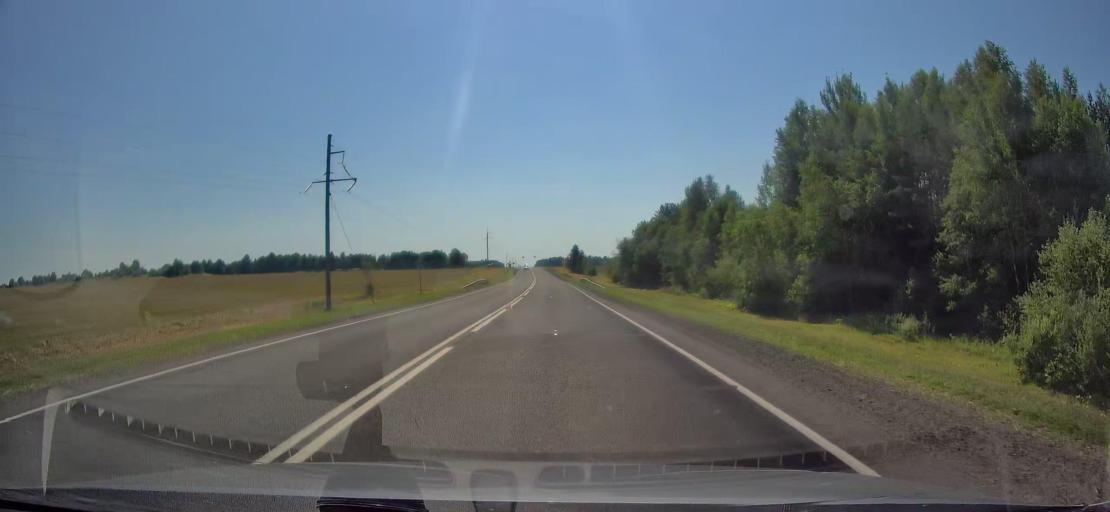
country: RU
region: Vologda
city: Sazonovo
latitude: 59.0578
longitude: 35.3216
